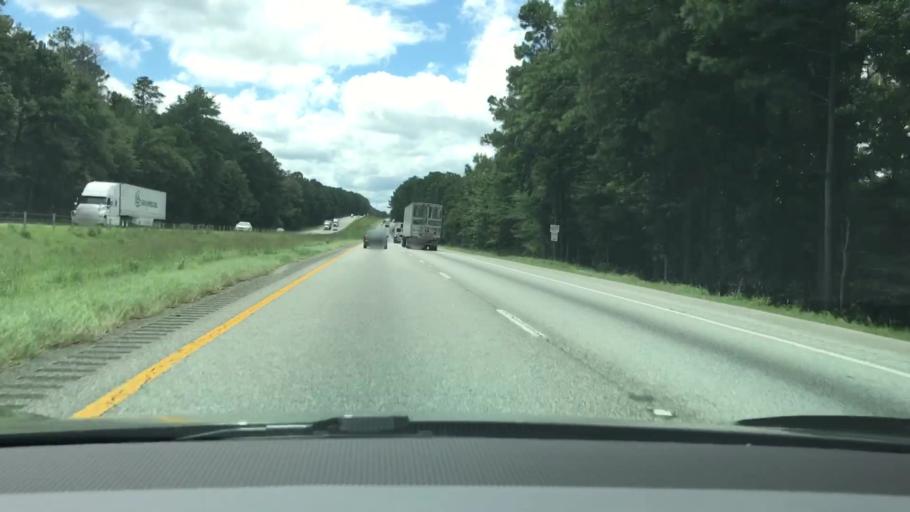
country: US
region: Alabama
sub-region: Chambers County
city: Huguley
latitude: 32.7845
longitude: -85.2462
